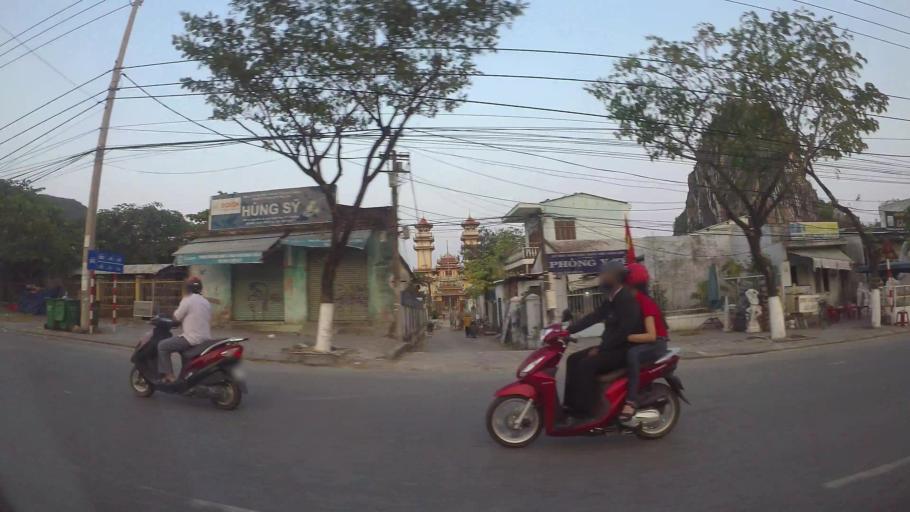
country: VN
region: Da Nang
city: Ngu Hanh Son
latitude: 16.0014
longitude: 108.2598
